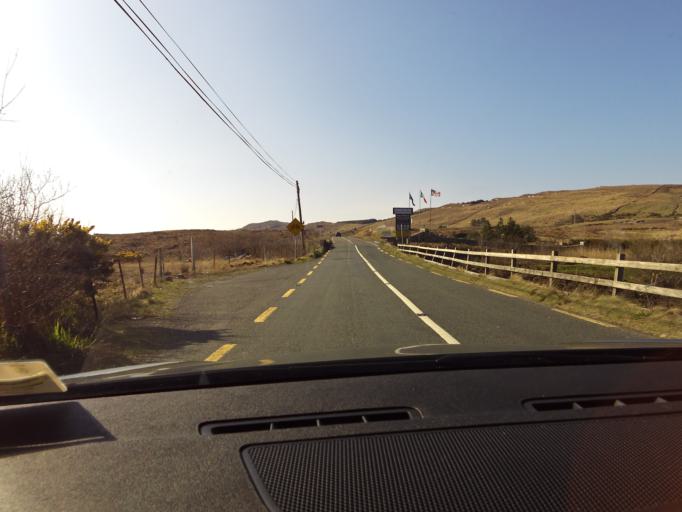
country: IE
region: Connaught
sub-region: County Galway
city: Clifden
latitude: 53.4779
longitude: -9.9119
